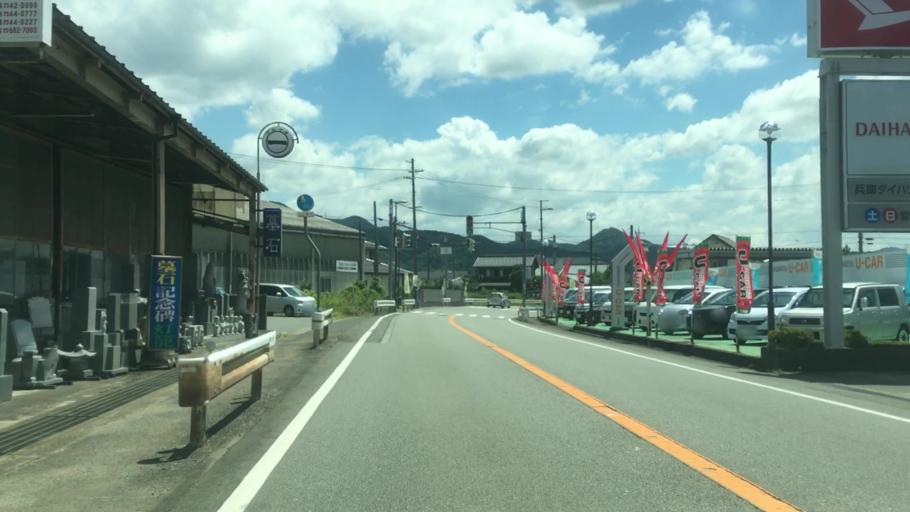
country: JP
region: Hyogo
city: Toyooka
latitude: 35.4897
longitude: 134.7999
